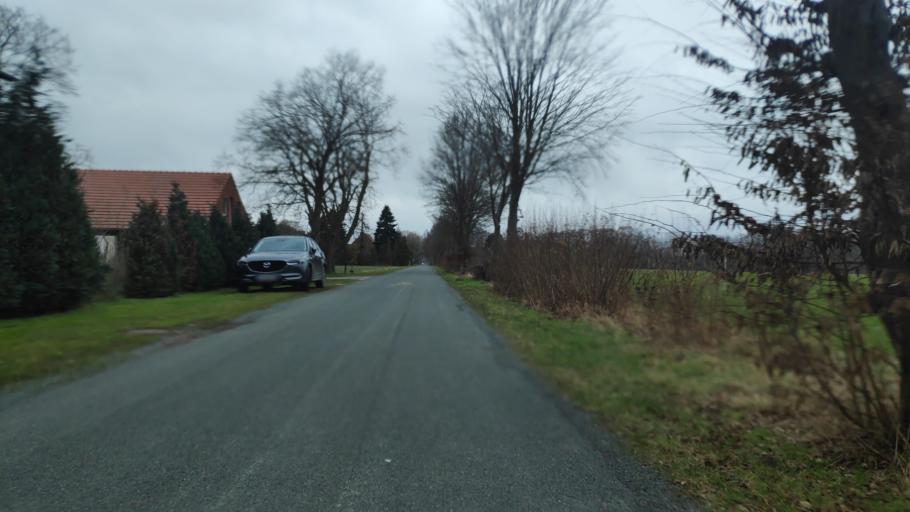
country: DE
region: North Rhine-Westphalia
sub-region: Regierungsbezirk Detmold
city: Hille
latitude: 52.3734
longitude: 8.7745
